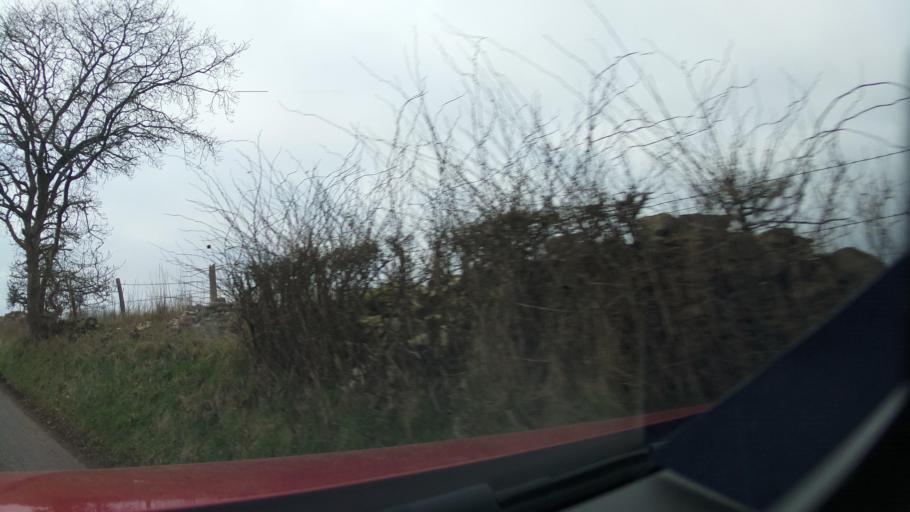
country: GB
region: England
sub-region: Wiltshire
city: Nettleton
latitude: 51.4836
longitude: -2.2586
